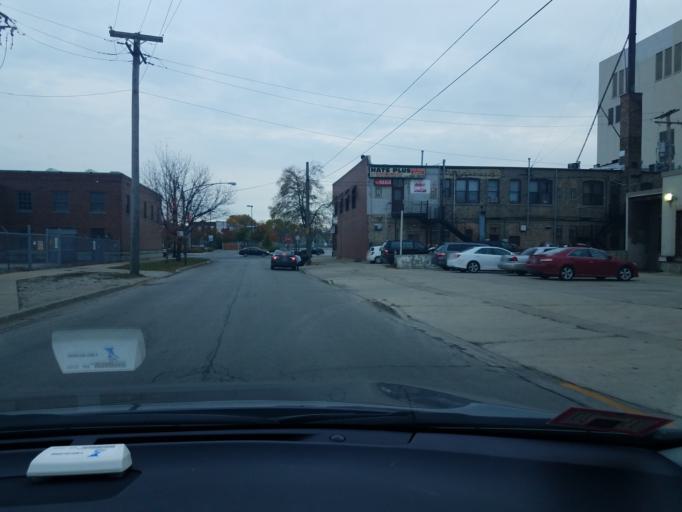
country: US
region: Illinois
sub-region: Cook County
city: Lincolnwood
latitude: 41.9542
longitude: -87.7456
